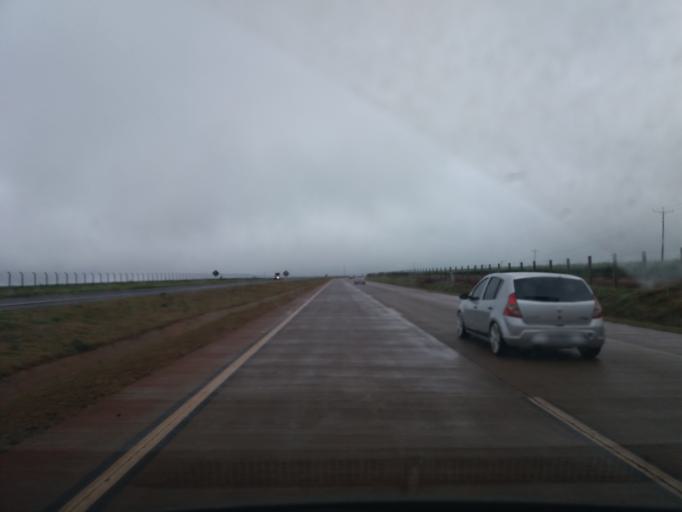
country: BR
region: Parana
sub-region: Cascavel
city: Cascavel
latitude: -25.1314
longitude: -53.5859
